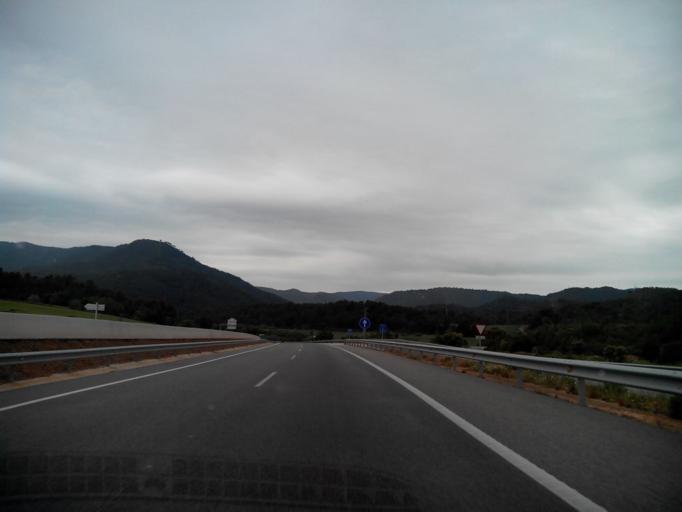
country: ES
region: Catalonia
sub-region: Provincia de Barcelona
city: Rajadell
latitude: 41.7387
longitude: 1.7072
